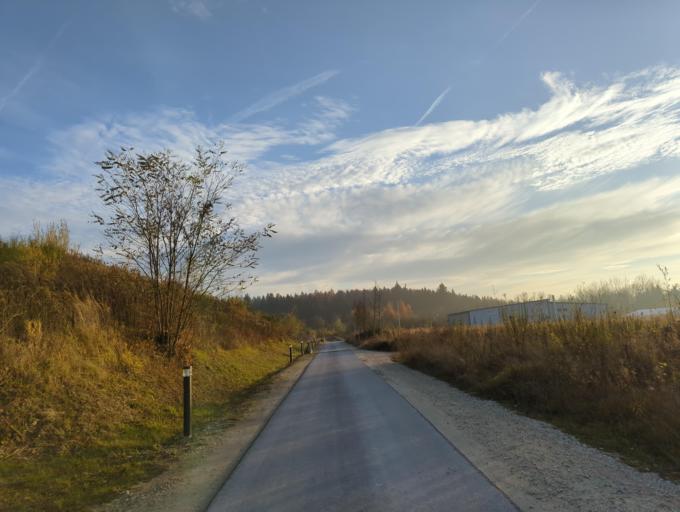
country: DE
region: Bavaria
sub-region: Swabia
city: Wasserburg
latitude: 48.4255
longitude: 10.3138
